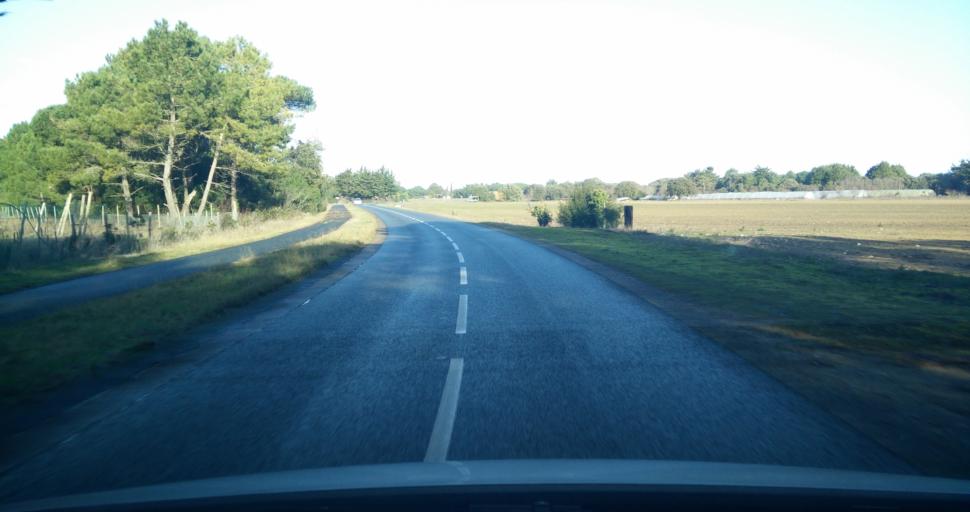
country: FR
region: Poitou-Charentes
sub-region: Departement de la Charente-Maritime
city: La Flotte
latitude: 46.1745
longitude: -1.3300
